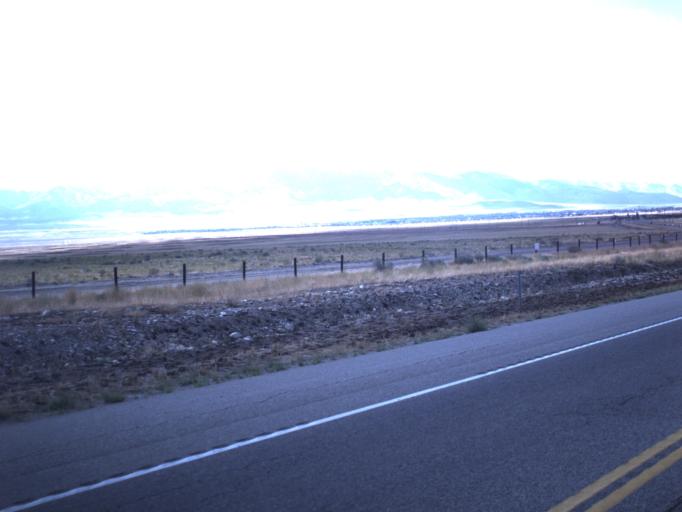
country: US
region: Utah
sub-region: Tooele County
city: Tooele
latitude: 40.5589
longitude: -112.3517
